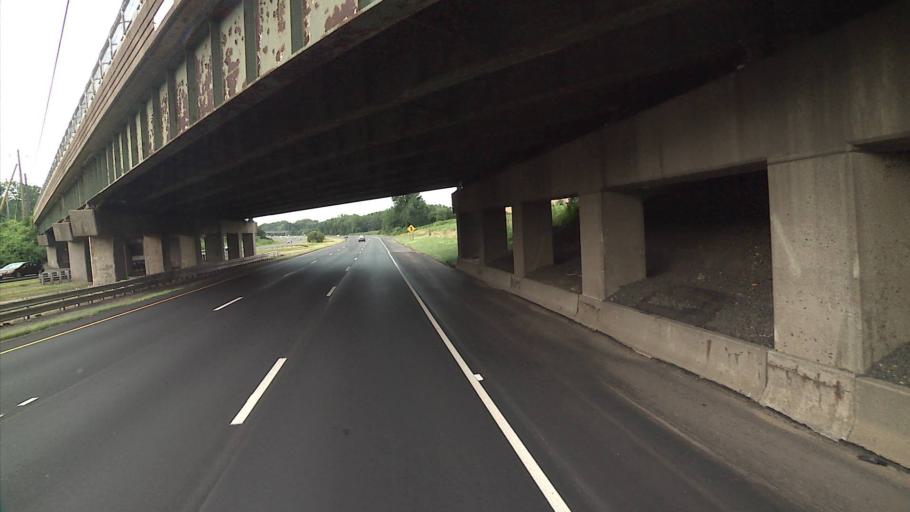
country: US
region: Connecticut
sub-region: Hartford County
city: Plainville
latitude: 41.6127
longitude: -72.8989
